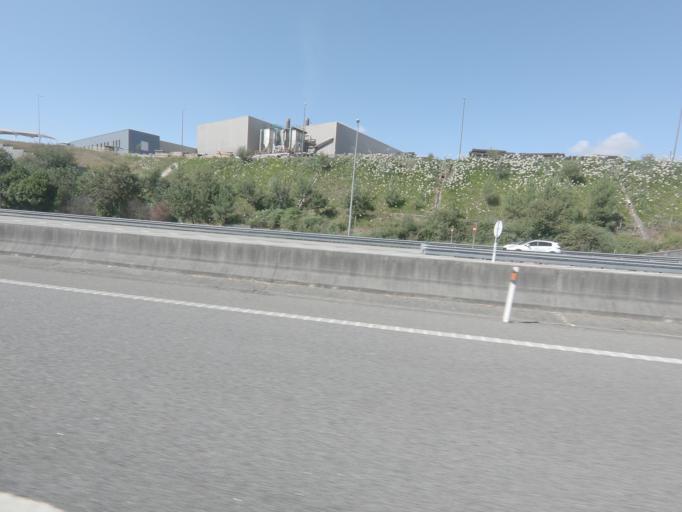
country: PT
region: Porto
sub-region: Valongo
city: Campo
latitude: 41.1784
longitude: -8.4427
